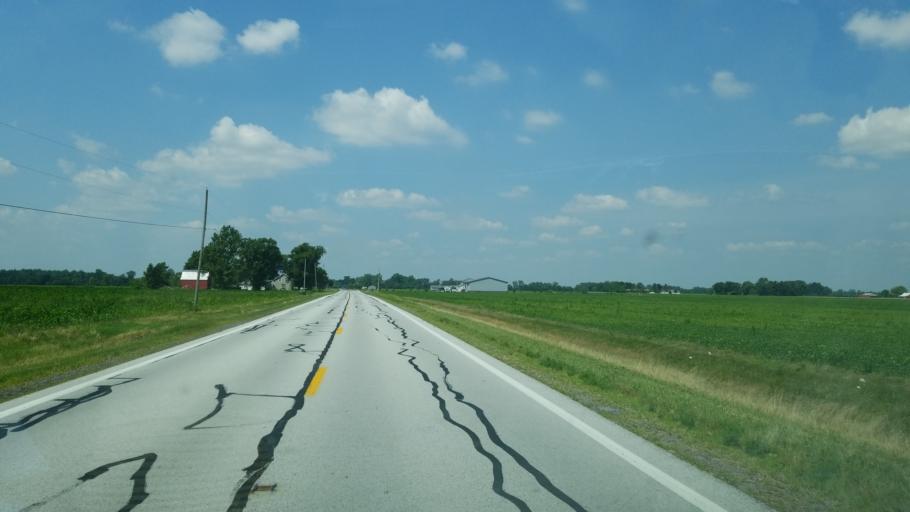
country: US
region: Ohio
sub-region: Henry County
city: Deshler
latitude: 41.2846
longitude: -83.8731
